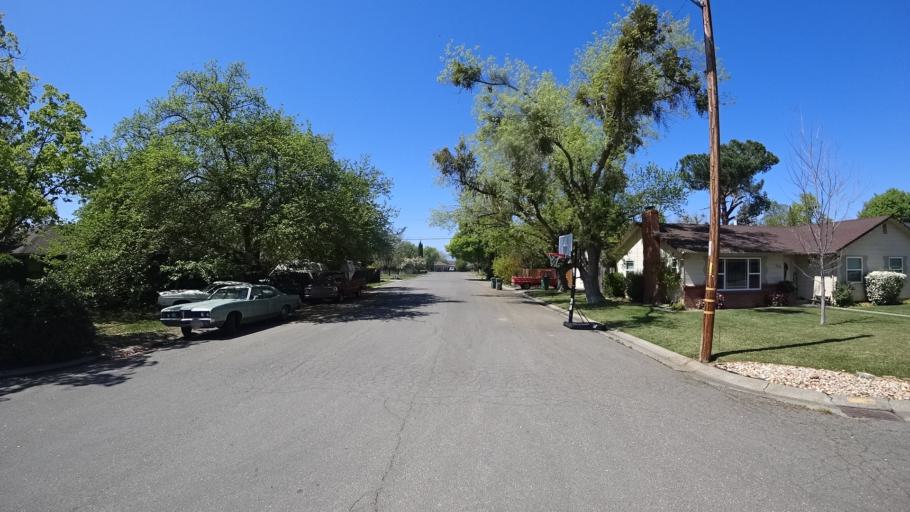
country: US
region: California
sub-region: Glenn County
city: Willows
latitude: 39.5254
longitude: -122.2057
